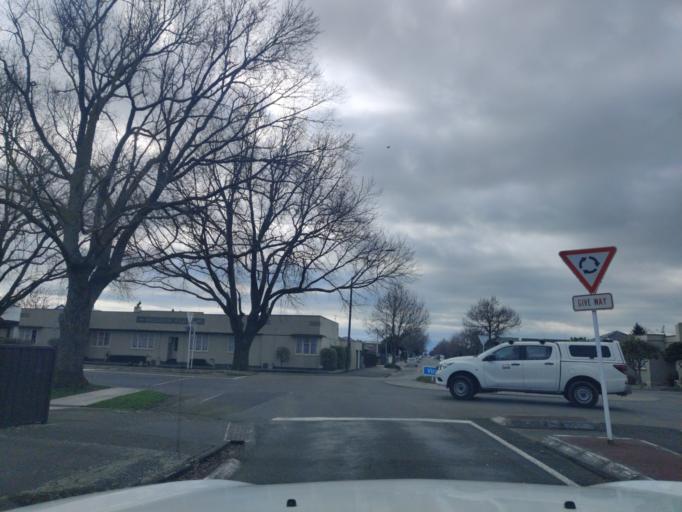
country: NZ
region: Manawatu-Wanganui
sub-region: Palmerston North City
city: Palmerston North
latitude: -40.3556
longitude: 175.6221
